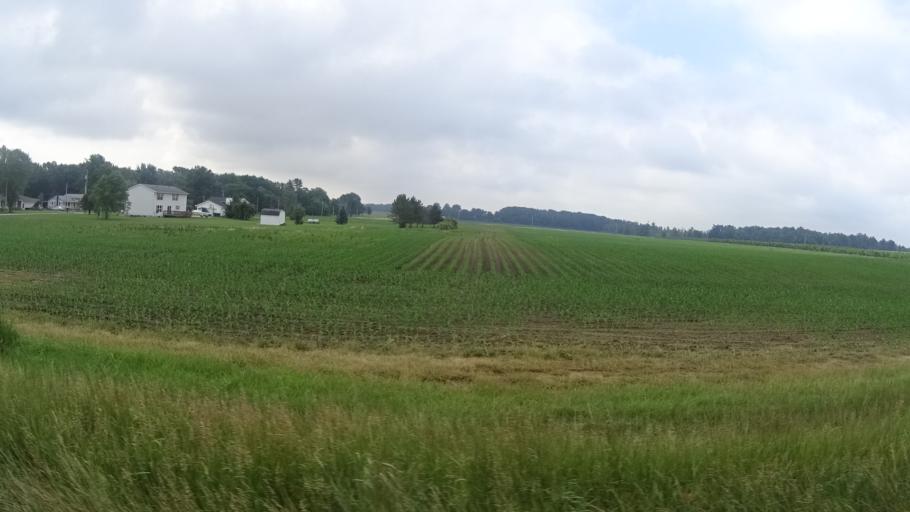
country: US
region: Ohio
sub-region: Huron County
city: Wakeman
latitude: 41.3054
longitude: -82.4827
